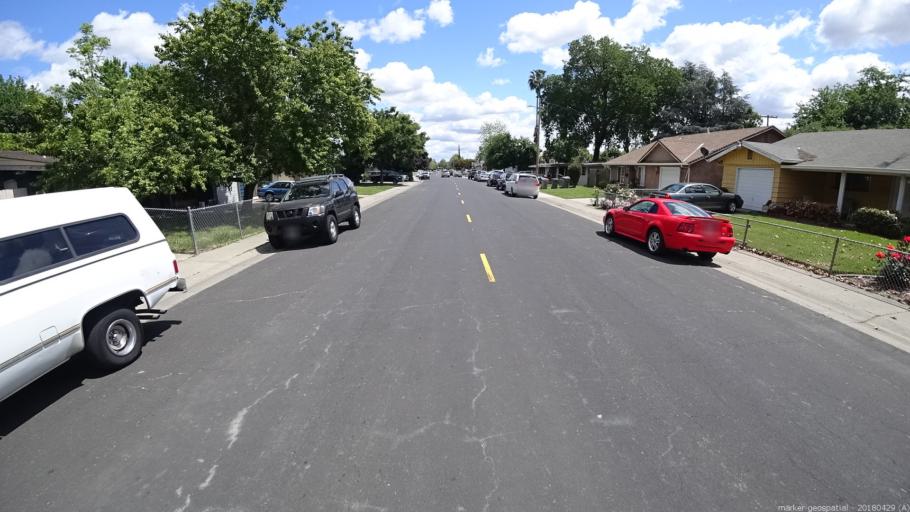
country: US
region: California
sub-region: Yolo County
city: West Sacramento
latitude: 38.5924
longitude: -121.5316
